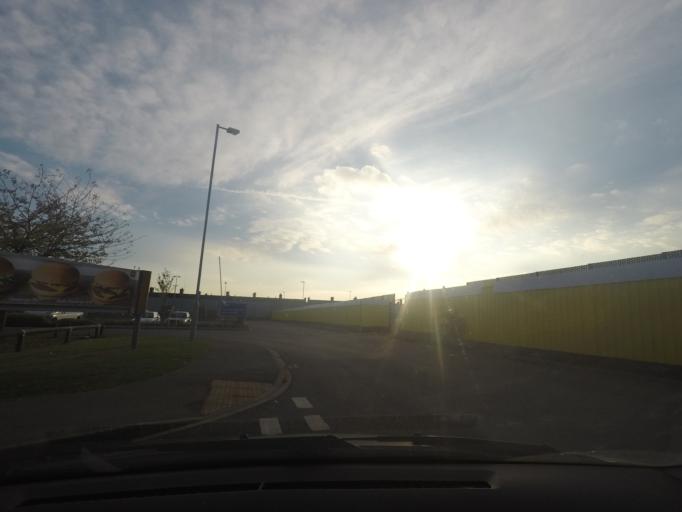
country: GB
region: England
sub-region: North East Lincolnshire
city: Grimbsy
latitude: 53.5746
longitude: -0.0983
